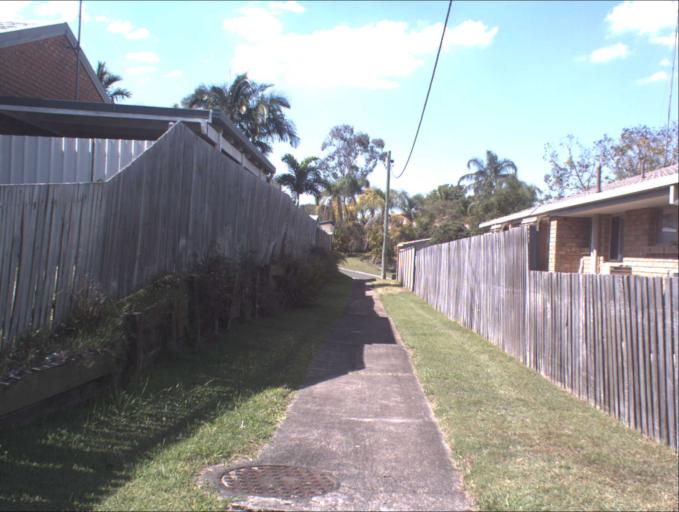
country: AU
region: Queensland
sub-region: Logan
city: Waterford West
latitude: -27.7015
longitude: 153.1665
